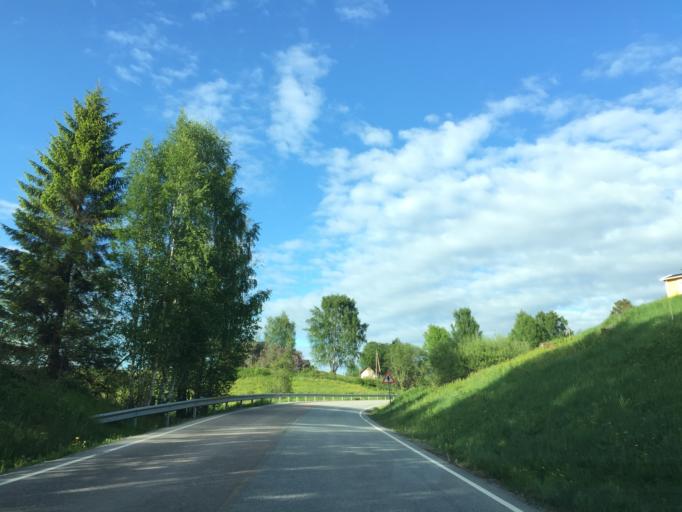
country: NO
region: Akershus
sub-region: Sorum
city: Sorumsand
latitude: 59.9861
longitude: 11.2804
